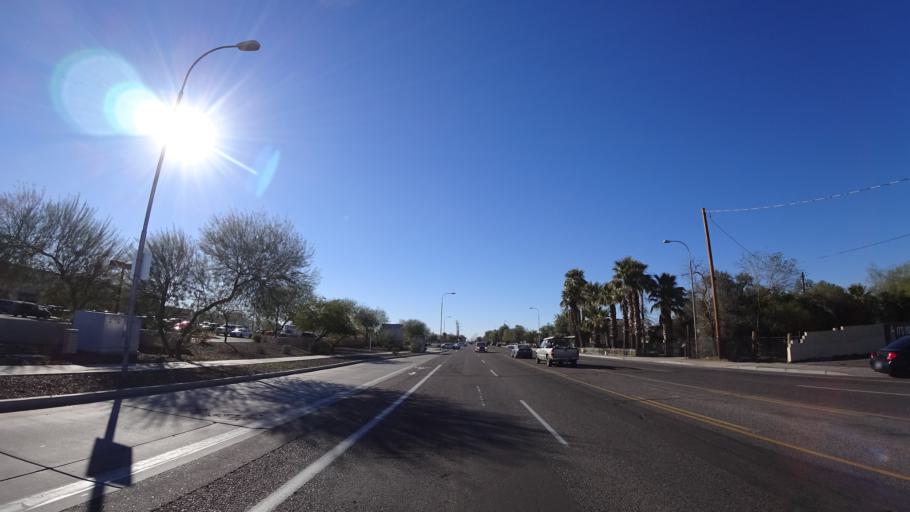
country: US
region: Arizona
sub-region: Maricopa County
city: Phoenix
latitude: 33.3921
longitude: -112.0834
